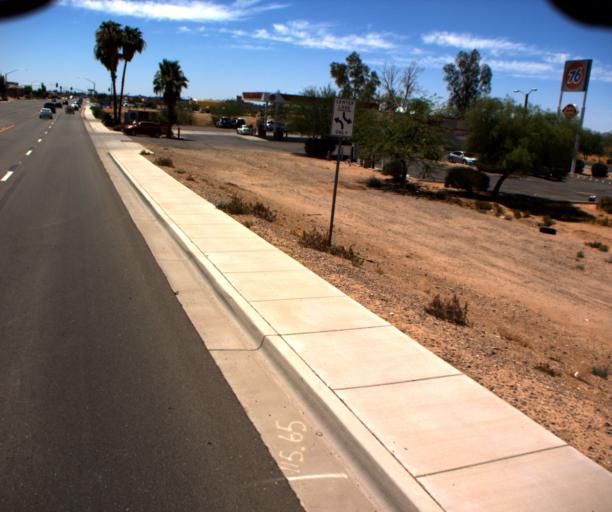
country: US
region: Arizona
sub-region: Pinal County
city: Casa Grande
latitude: 32.8798
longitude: -111.6897
